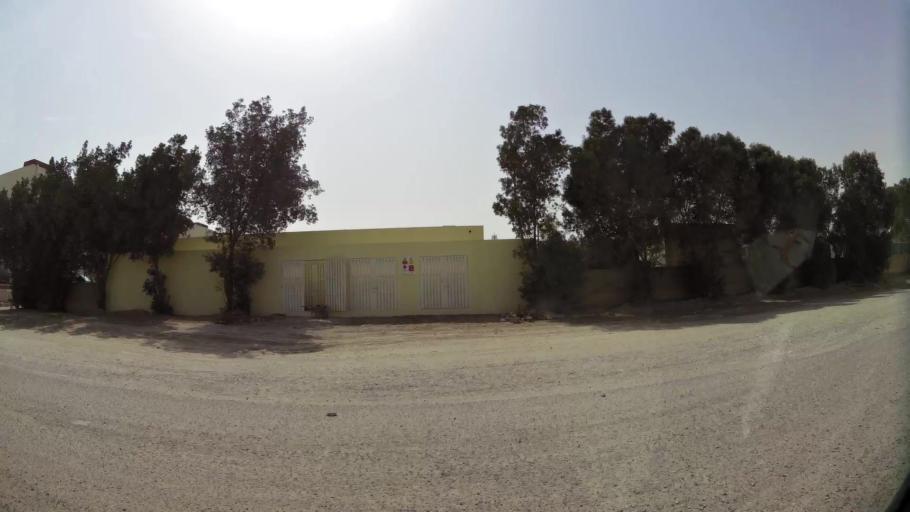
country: QA
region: Al Wakrah
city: Al Wukayr
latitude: 25.1686
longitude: 51.4621
